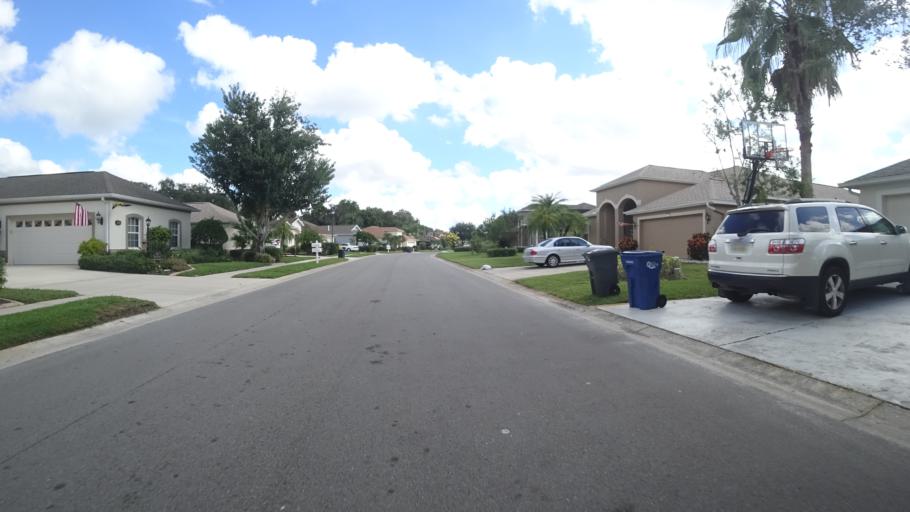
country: US
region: Florida
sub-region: Manatee County
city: Ellenton
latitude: 27.4950
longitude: -82.4386
